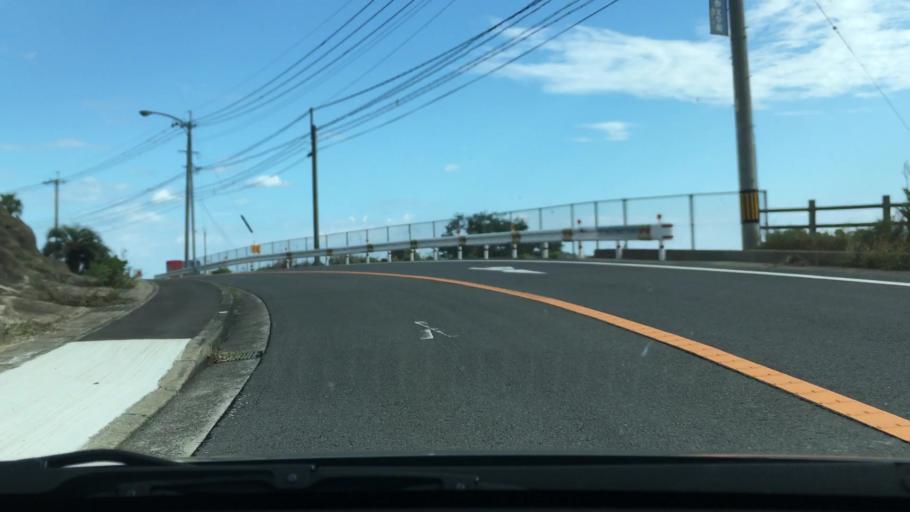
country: JP
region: Nagasaki
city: Togitsu
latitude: 32.8234
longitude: 129.7239
